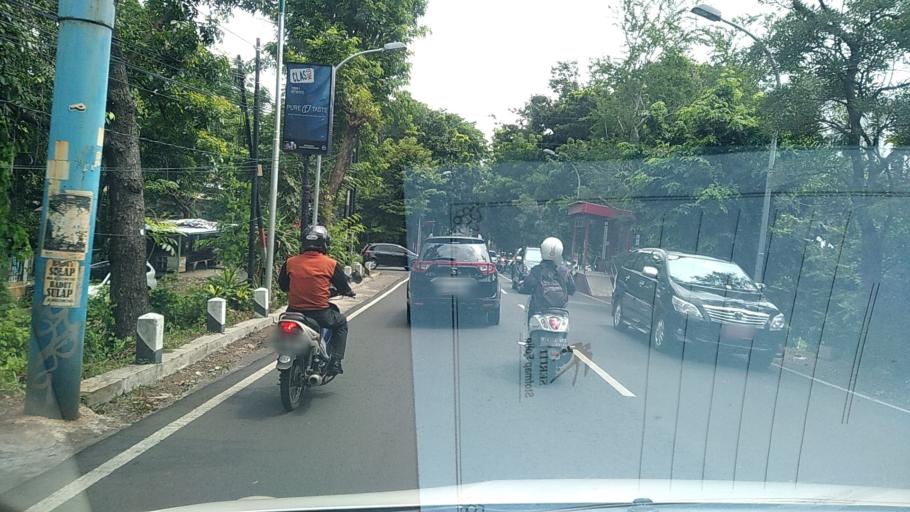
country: ID
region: Central Java
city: Semarang
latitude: -7.0012
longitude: 110.4174
